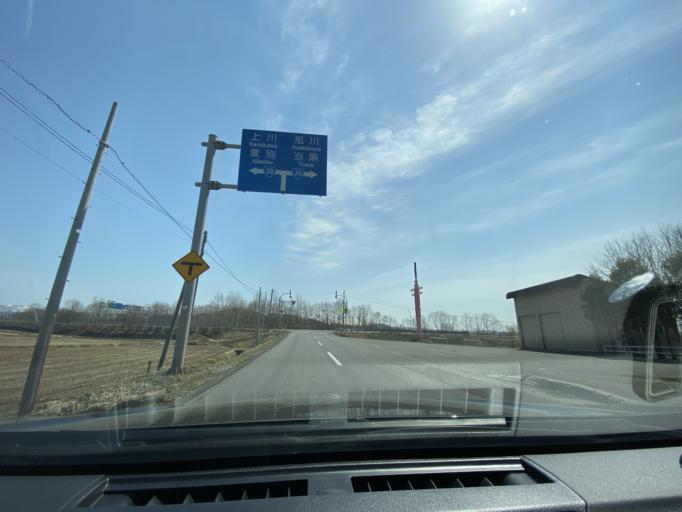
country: JP
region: Hokkaido
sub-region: Asahikawa-shi
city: Asahikawa
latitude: 43.8974
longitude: 142.5253
